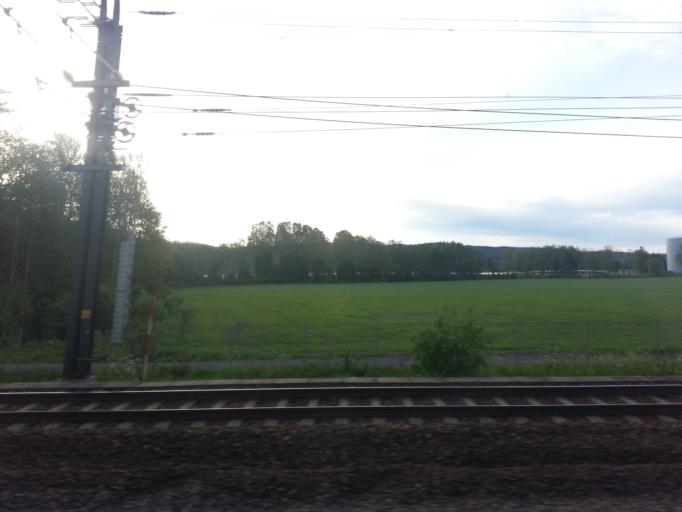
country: NO
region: Akershus
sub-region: Skedsmo
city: Lillestrom
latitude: 59.9738
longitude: 11.0698
